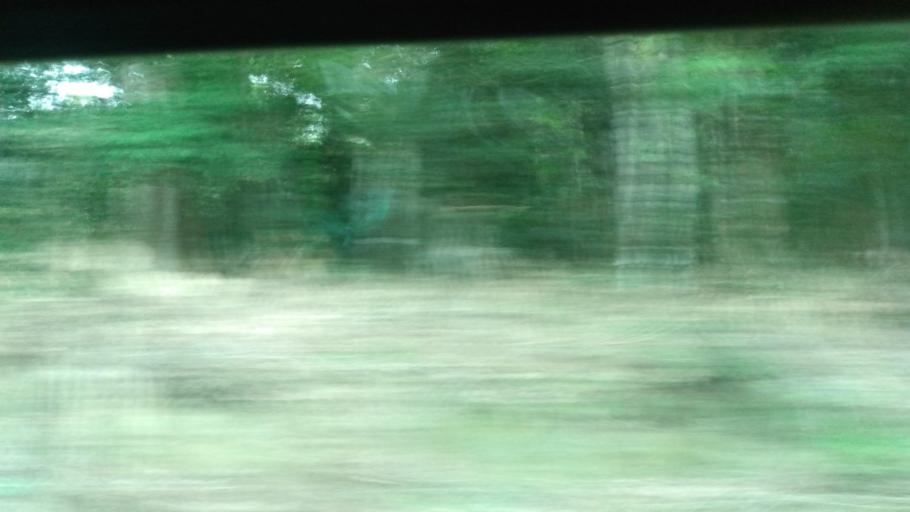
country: BR
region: Pernambuco
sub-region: Maraial
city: Maraial
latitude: -8.7806
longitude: -35.9131
